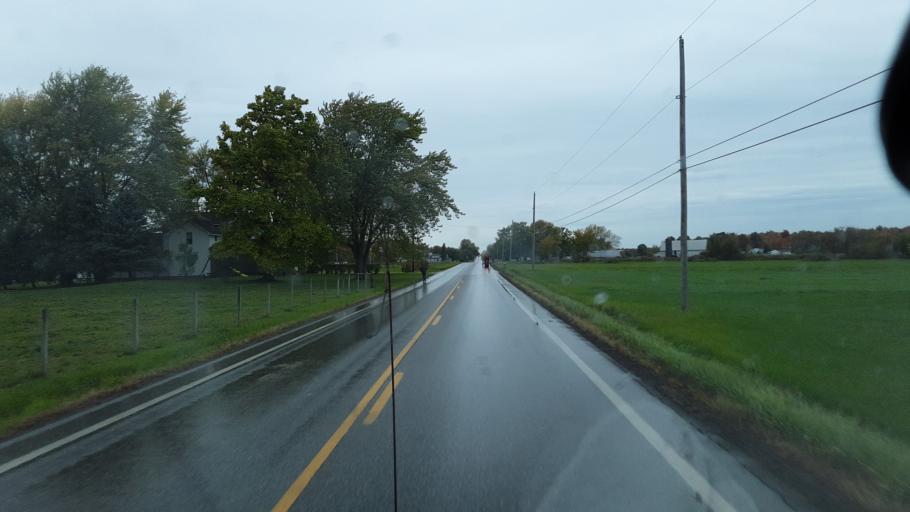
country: US
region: Ohio
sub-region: Geauga County
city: Middlefield
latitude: 41.3983
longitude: -81.0897
